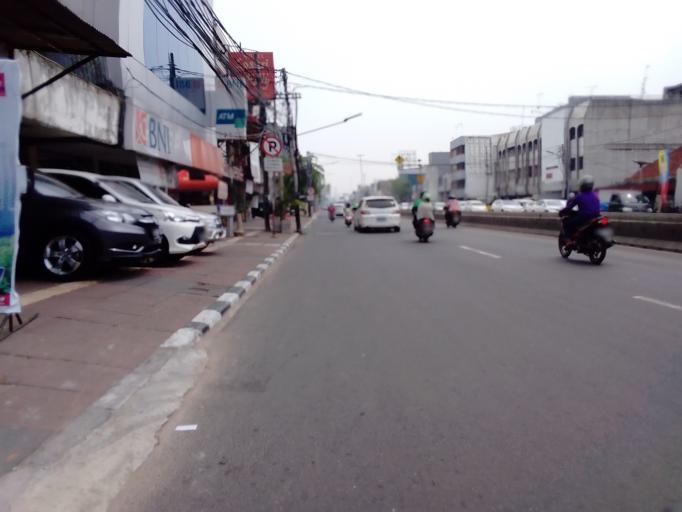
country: ID
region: Jakarta Raya
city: Jakarta
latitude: -6.1658
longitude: 106.8098
